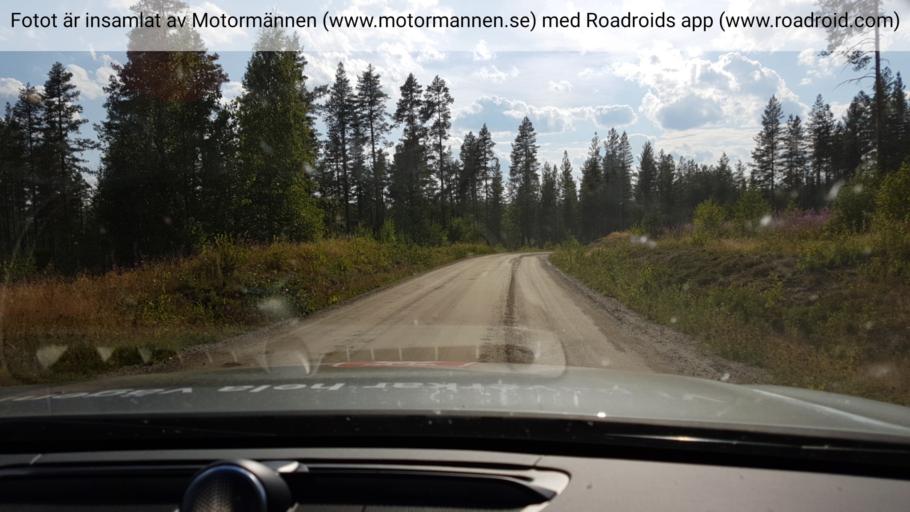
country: SE
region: Vaesternorrland
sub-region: Solleftea Kommun
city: As
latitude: 63.7848
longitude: 16.3884
